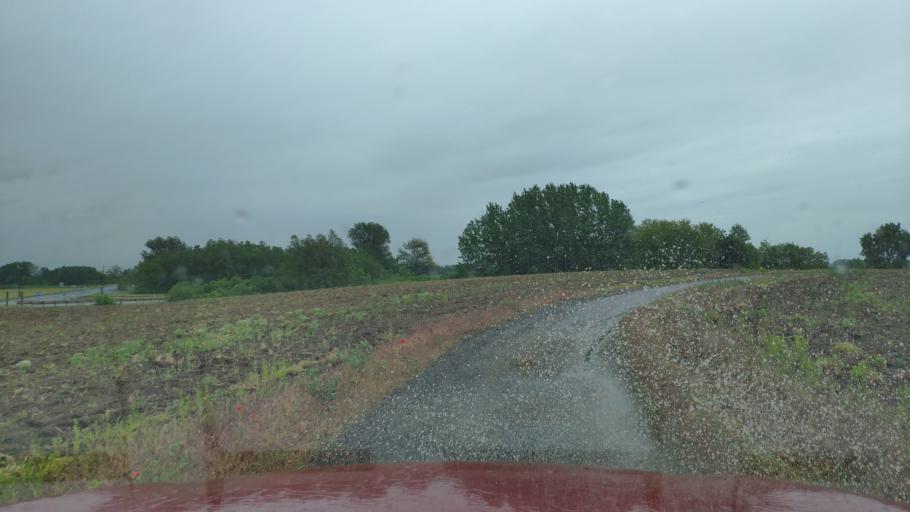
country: SK
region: Kosicky
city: Cierna nad Tisou
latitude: 48.4295
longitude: 22.0195
